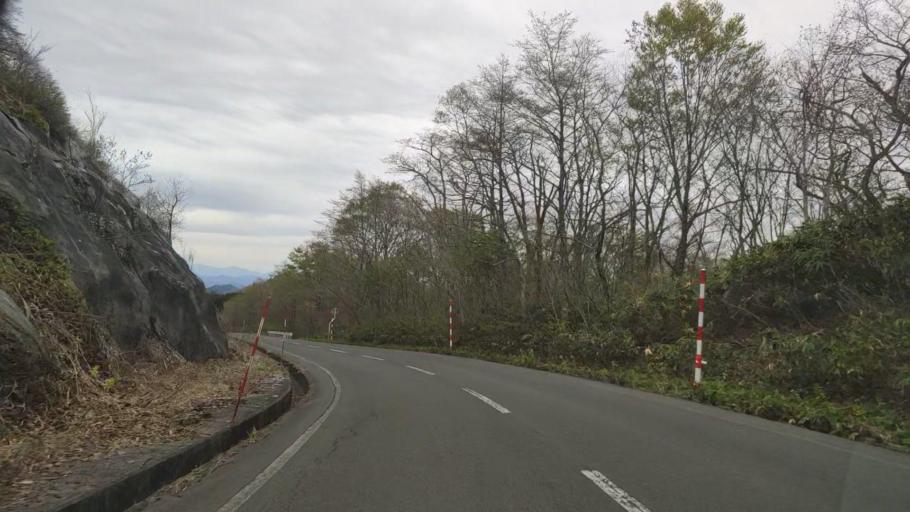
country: JP
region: Akita
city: Hanawa
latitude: 40.4014
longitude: 140.8028
